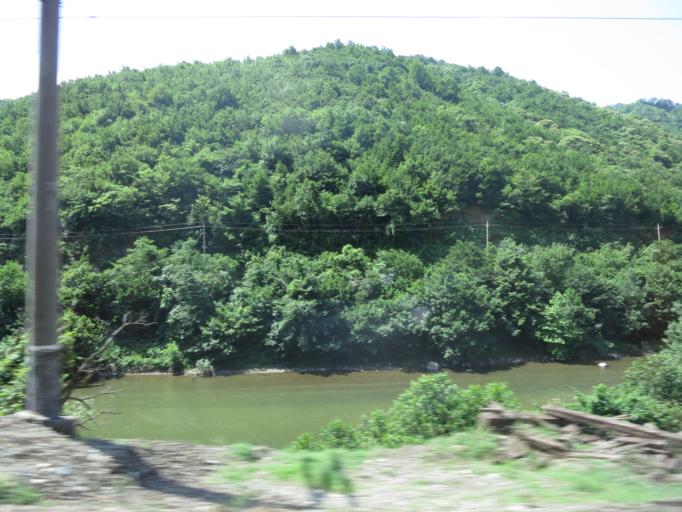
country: GE
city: Shorapani
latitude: 42.0834
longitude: 43.1501
